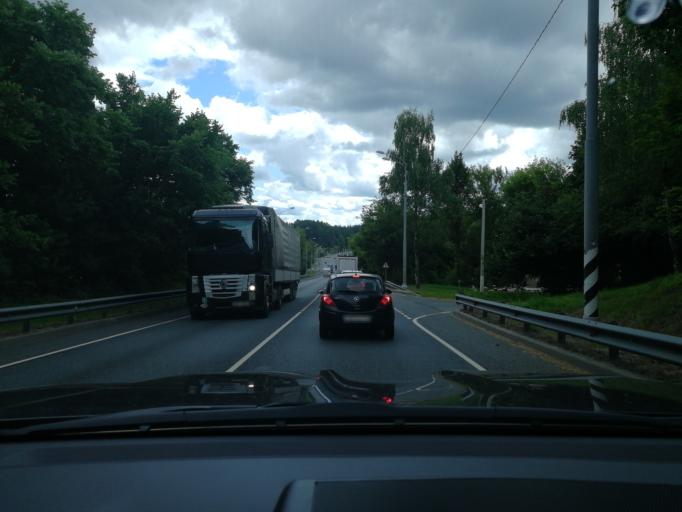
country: RU
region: Moskovskaya
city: Popovo
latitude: 55.0593
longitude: 37.7652
